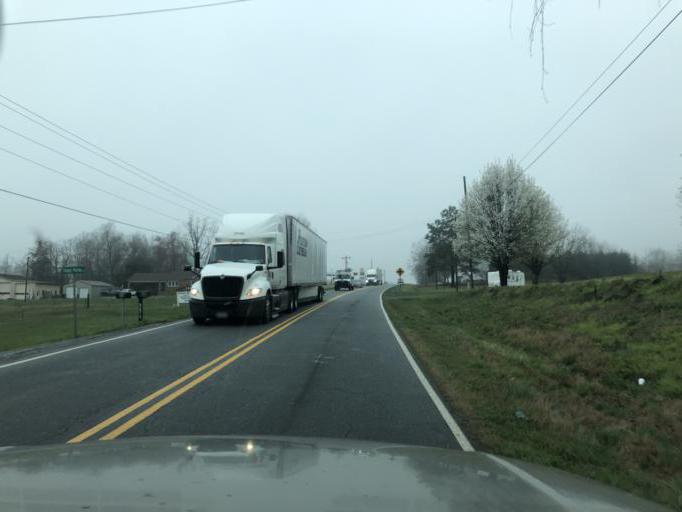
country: US
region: North Carolina
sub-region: Gaston County
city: Cherryville
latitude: 35.3494
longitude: -81.4460
